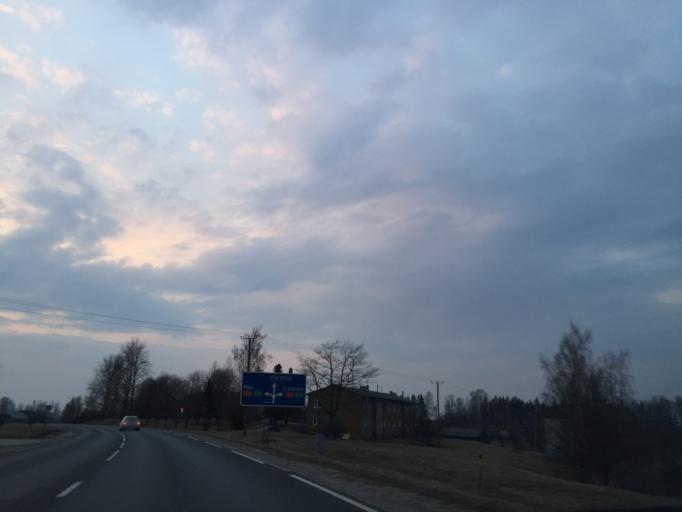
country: LV
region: Raunas
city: Rauna
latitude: 57.2777
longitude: 25.5019
